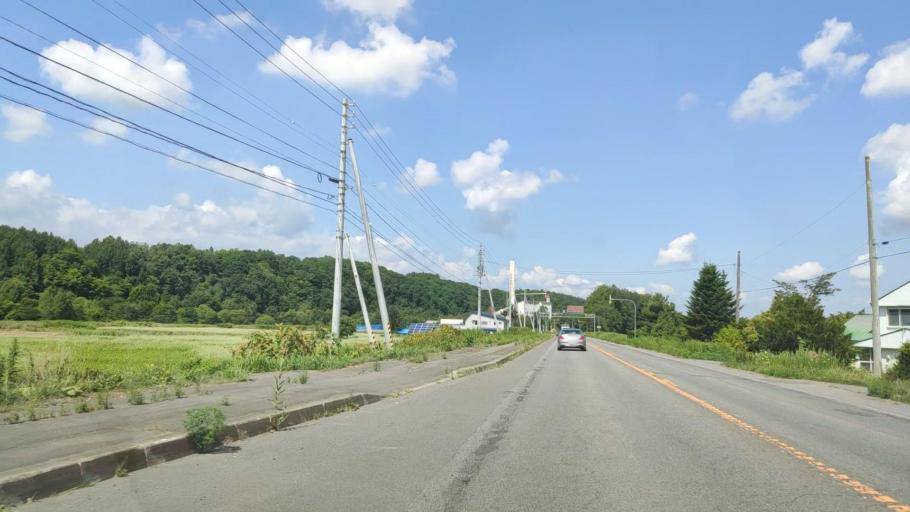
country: JP
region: Hokkaido
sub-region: Asahikawa-shi
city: Asahikawa
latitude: 43.6184
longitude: 142.4744
